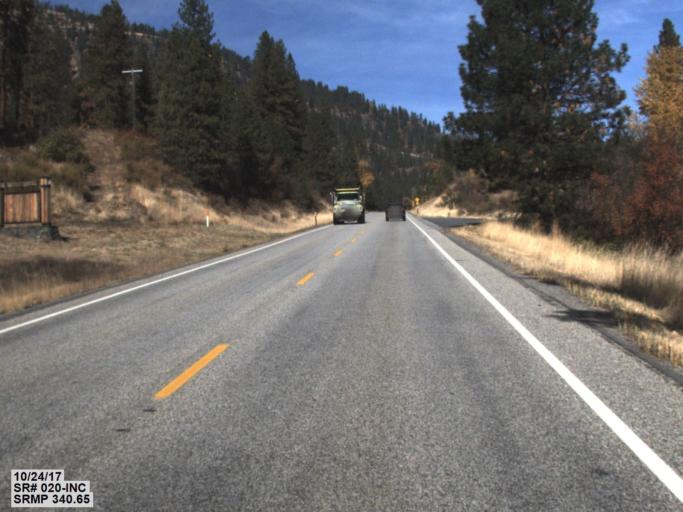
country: US
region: Washington
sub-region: Stevens County
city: Kettle Falls
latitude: 48.6113
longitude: -118.1384
